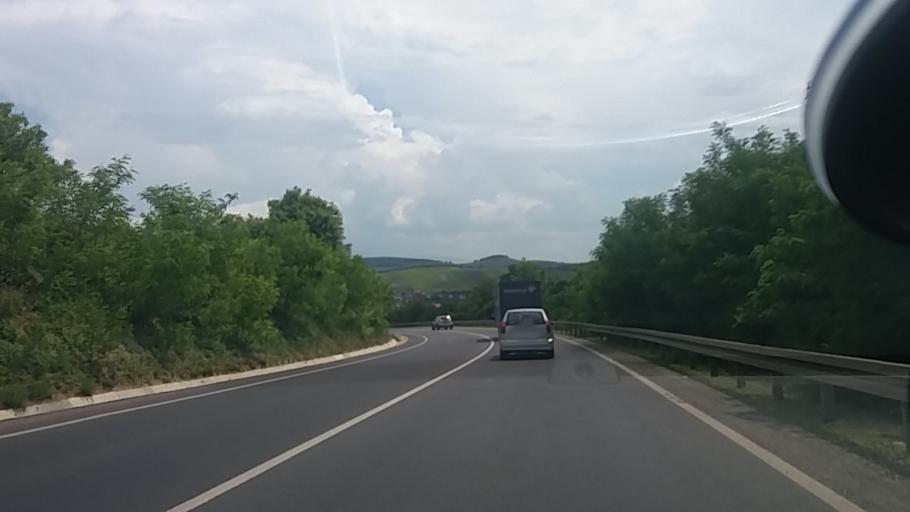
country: RO
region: Sibiu
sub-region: Comuna Sura Mare
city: Sura Mare
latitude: 45.8619
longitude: 24.1655
